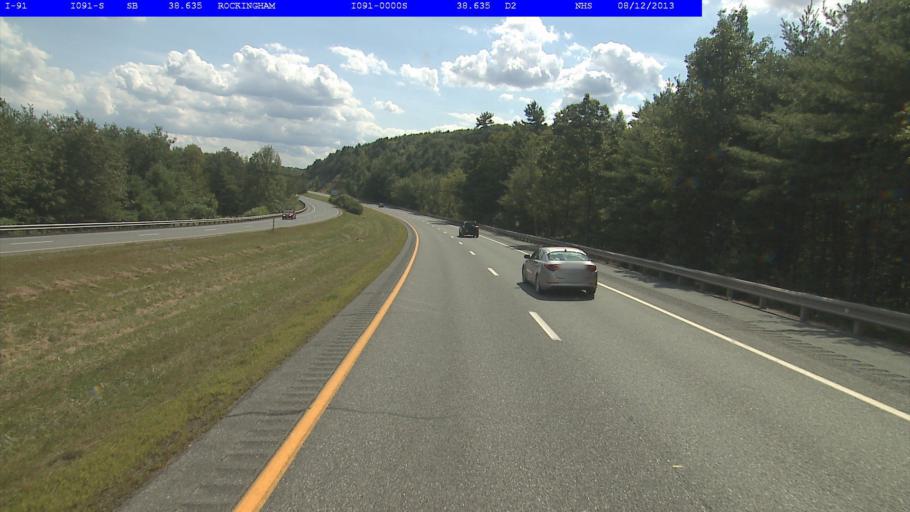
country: US
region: New Hampshire
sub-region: Sullivan County
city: Charlestown
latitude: 43.2270
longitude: -72.4526
